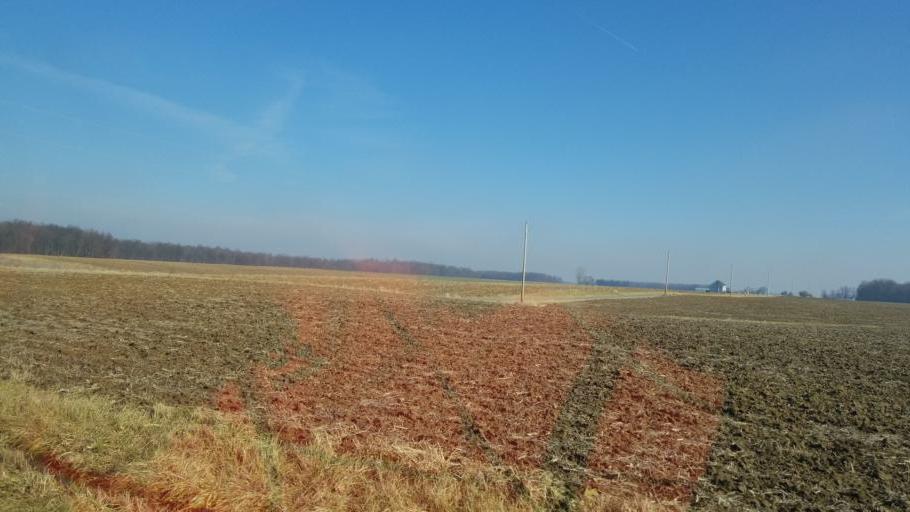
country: US
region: Ohio
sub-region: Seneca County
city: Tiffin
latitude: 40.9720
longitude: -83.0743
